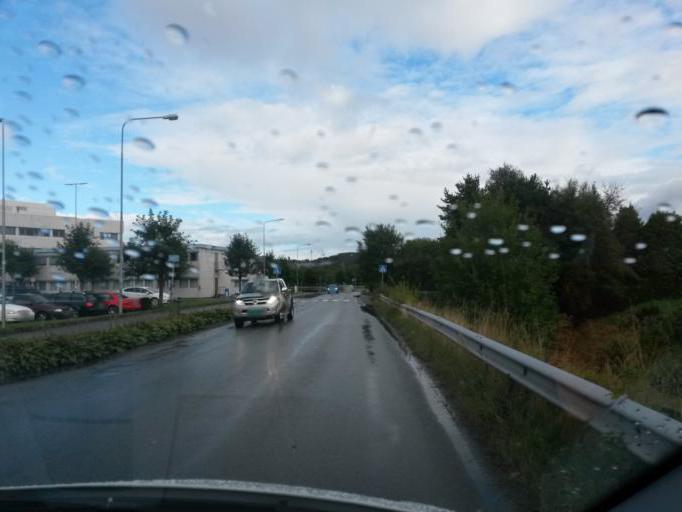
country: NO
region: Rogaland
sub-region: Sandnes
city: Sandnes
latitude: 58.8867
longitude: 5.7237
